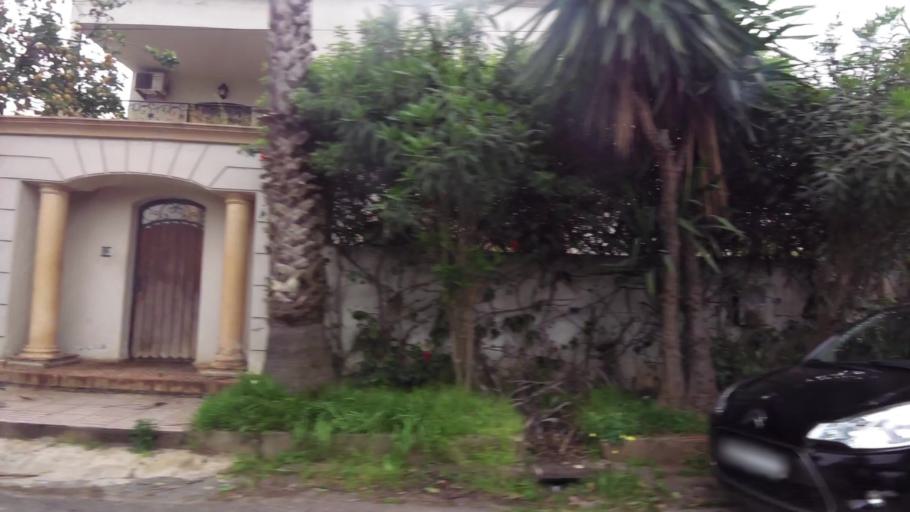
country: MA
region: Grand Casablanca
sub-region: Casablanca
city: Casablanca
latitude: 33.5804
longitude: -7.6558
